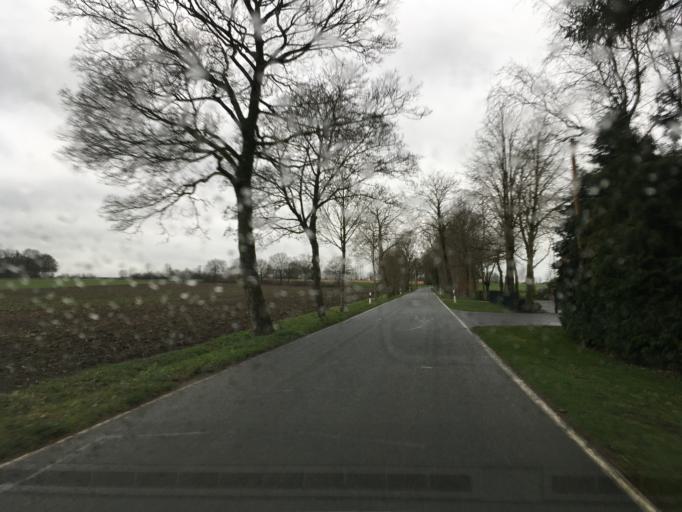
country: DE
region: North Rhine-Westphalia
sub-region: Regierungsbezirk Munster
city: Schoppingen
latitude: 52.0811
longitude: 7.1683
